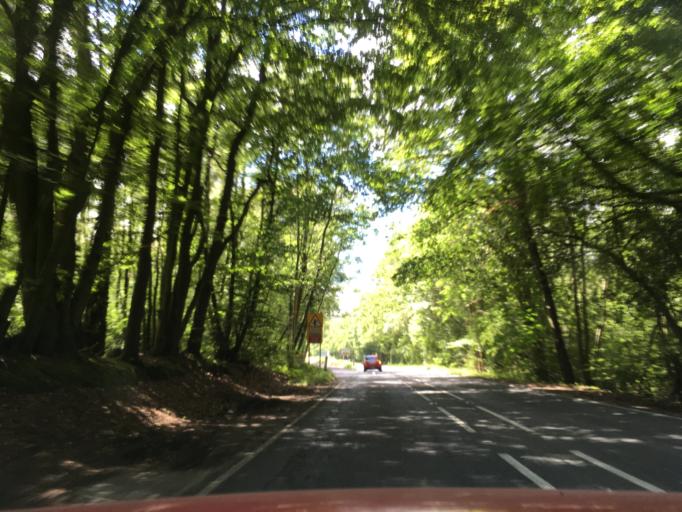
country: GB
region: England
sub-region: Hampshire
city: Highclere
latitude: 51.3546
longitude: -1.3692
